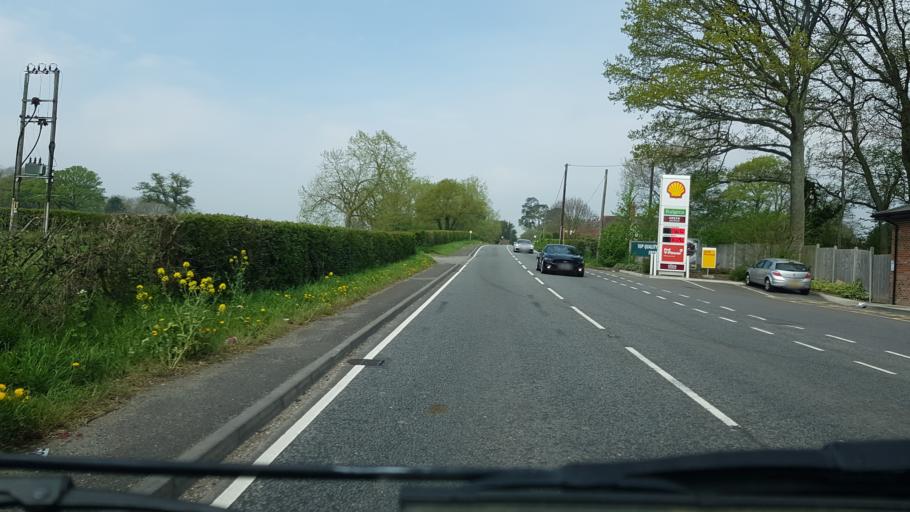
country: GB
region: England
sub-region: Hampshire
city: Kingsclere
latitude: 51.3323
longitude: -1.2557
